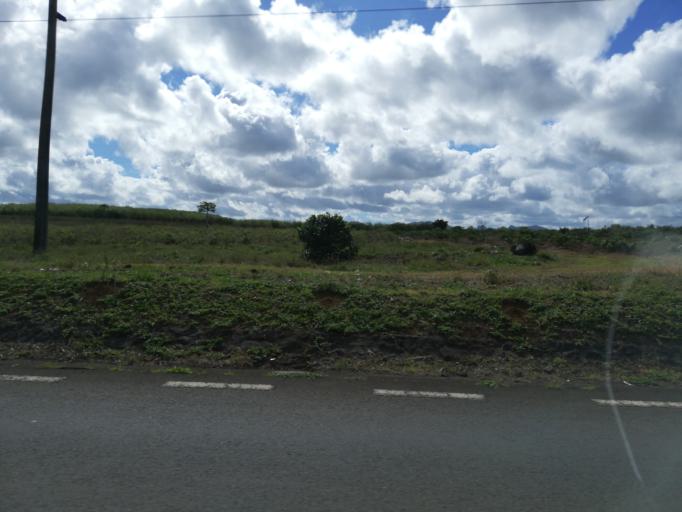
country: MU
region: Grand Port
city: Plaine Magnien
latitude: -20.4253
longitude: 57.6529
